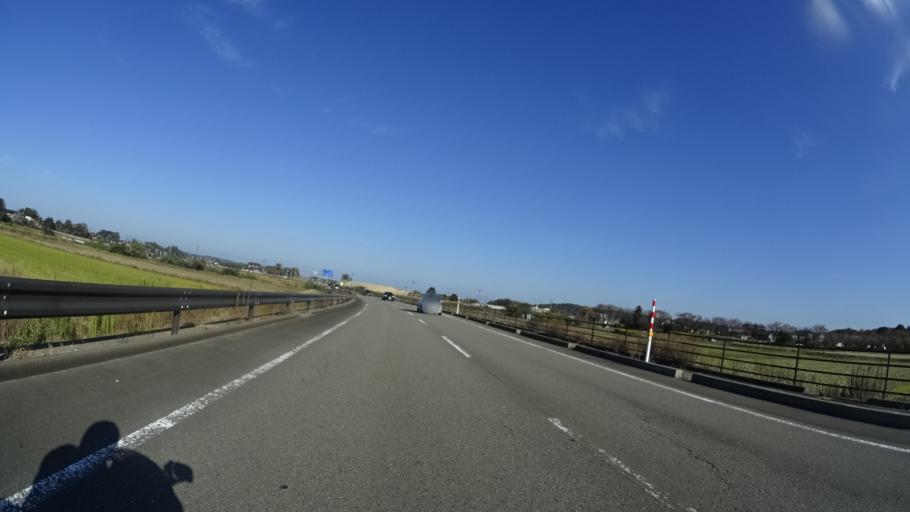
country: JP
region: Ishikawa
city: Komatsu
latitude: 36.2986
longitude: 136.3880
